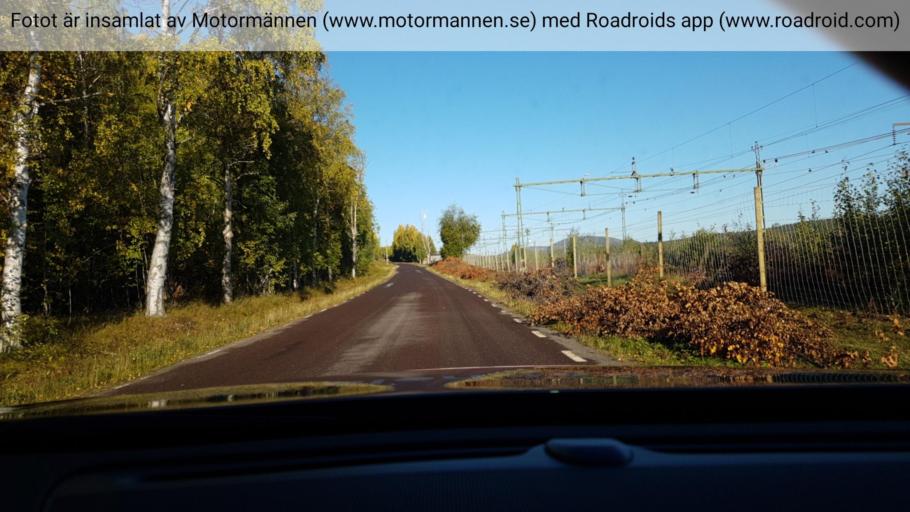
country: SE
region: Norrbotten
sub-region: Bodens Kommun
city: Boden
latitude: 66.1258
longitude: 21.3196
